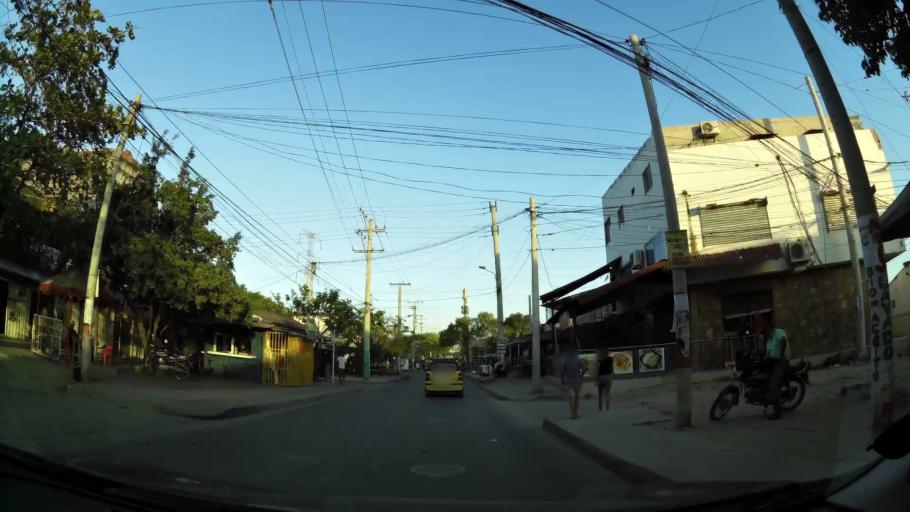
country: CO
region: Atlantico
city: Soledad
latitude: 10.9215
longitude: -74.7904
